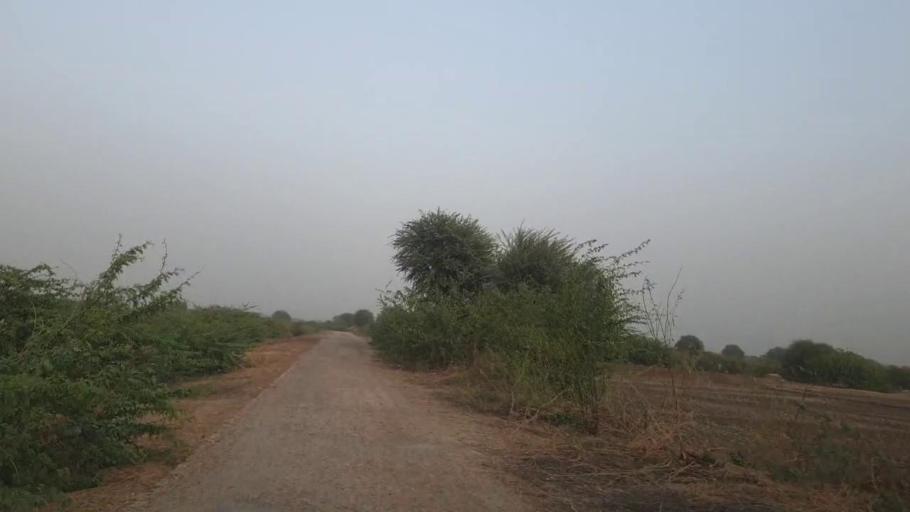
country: PK
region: Sindh
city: Kunri
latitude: 25.1193
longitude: 69.5532
